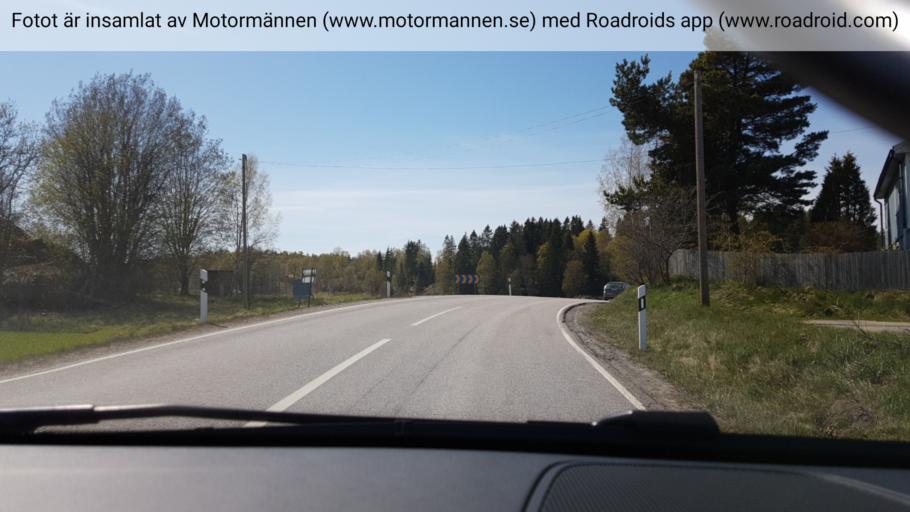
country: SE
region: Stockholm
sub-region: Nynashamns Kommun
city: Osmo
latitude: 58.9871
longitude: 17.8260
